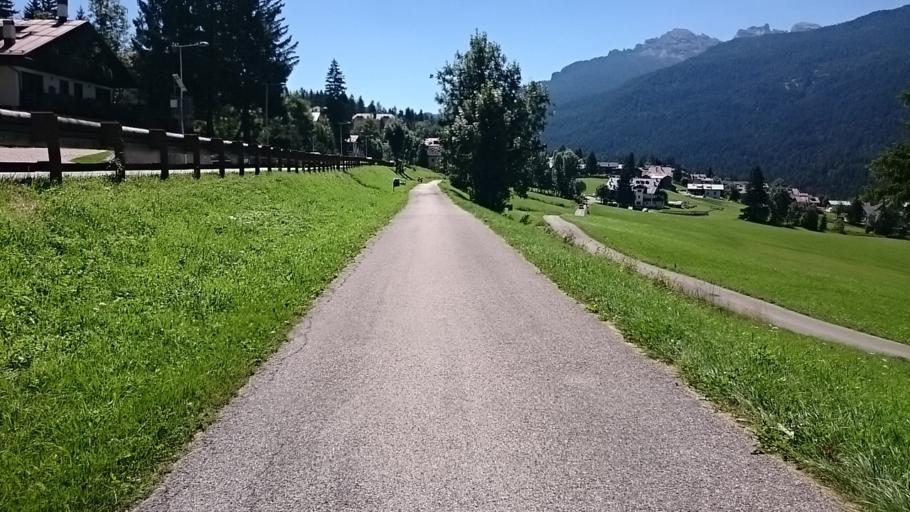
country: IT
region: Veneto
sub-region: Provincia di Belluno
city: Cortina d'Ampezzo
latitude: 46.5253
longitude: 12.1401
